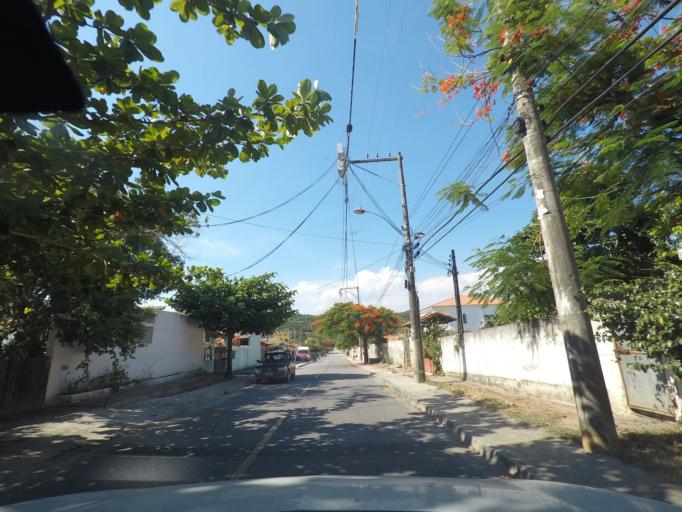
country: BR
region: Rio de Janeiro
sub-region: Niteroi
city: Niteroi
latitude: -22.9634
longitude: -42.9729
